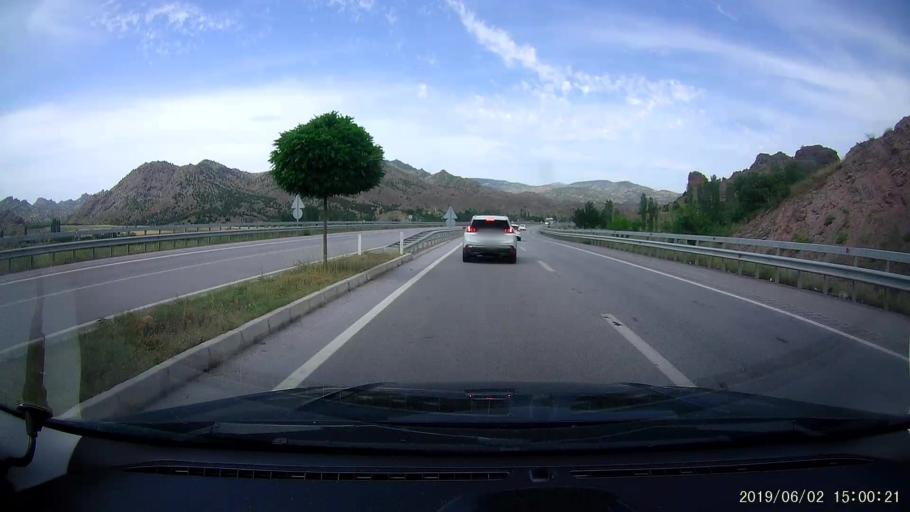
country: TR
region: Corum
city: Osmancik
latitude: 40.9778
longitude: 34.7111
